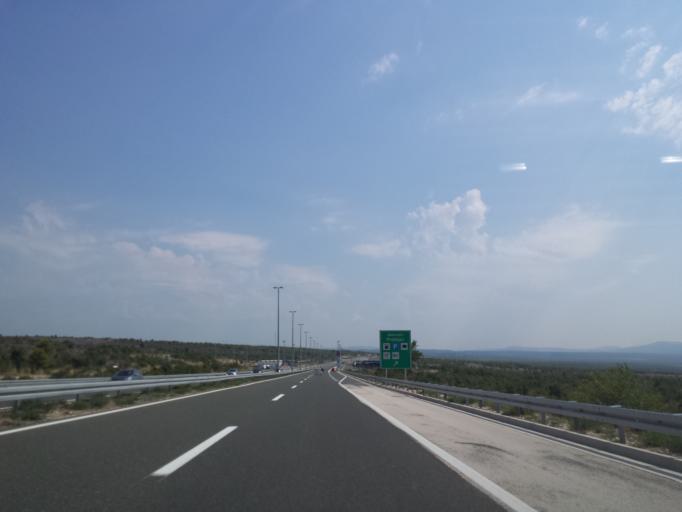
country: HR
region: Sibensko-Kniniska
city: Zaton
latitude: 43.8573
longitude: 15.8405
